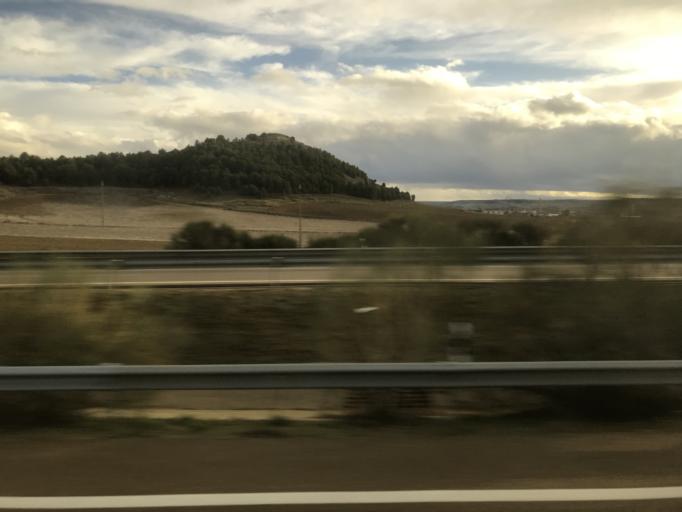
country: ES
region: Castille and Leon
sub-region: Provincia de Palencia
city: Villalobon
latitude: 42.0388
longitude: -4.5292
